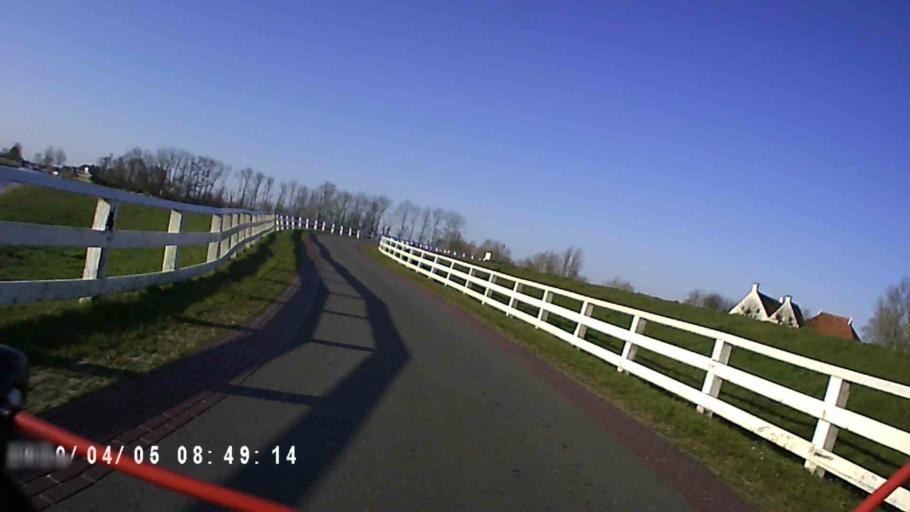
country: NL
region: Groningen
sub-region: Gemeente Winsum
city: Winsum
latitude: 53.3197
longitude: 6.4692
